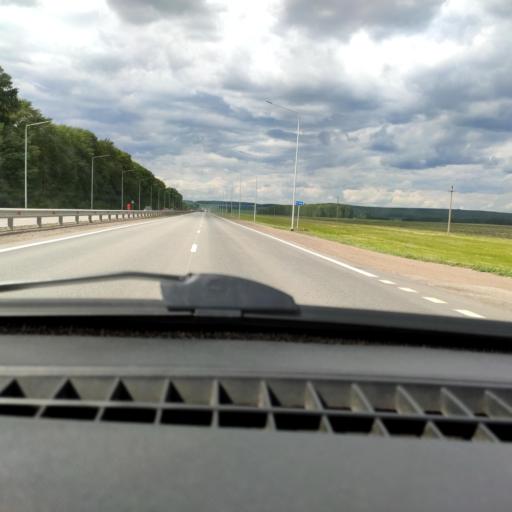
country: RU
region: Bashkortostan
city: Sterlitamak
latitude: 53.7813
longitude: 55.9433
